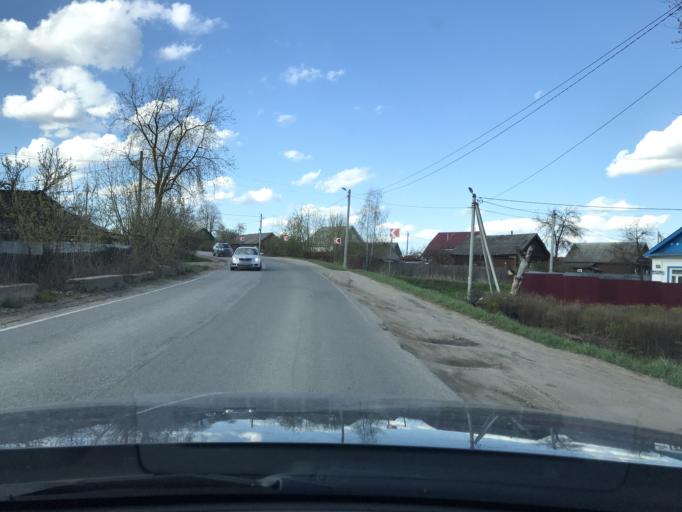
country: RU
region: Vladimir
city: Strunino
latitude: 56.3825
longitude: 38.5793
